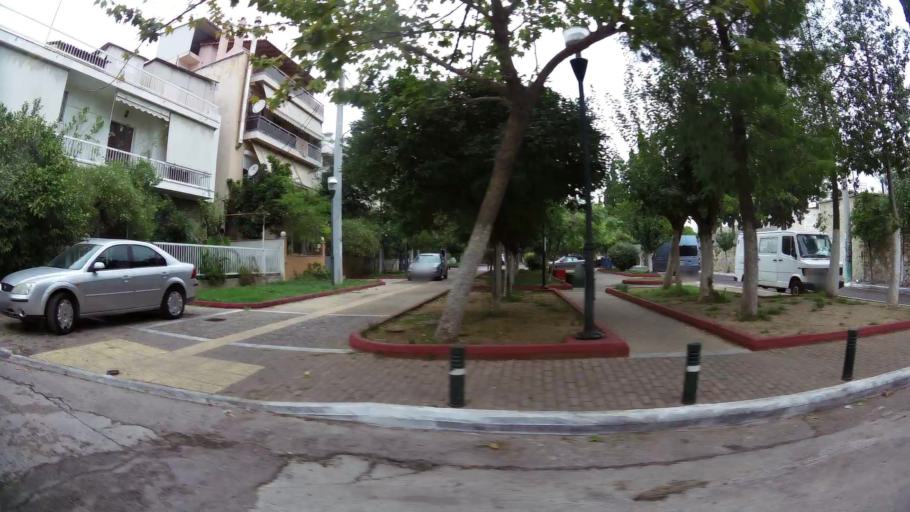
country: GR
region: Attica
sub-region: Nomarchia Athinas
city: Agia Varvara
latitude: 37.9830
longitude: 23.6637
